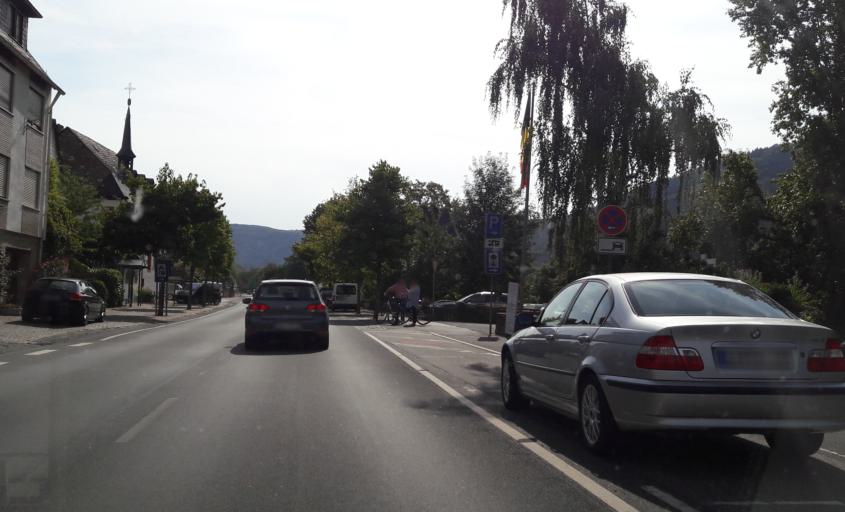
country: DE
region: Rheinland-Pfalz
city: Ediger-Eller
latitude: 50.0935
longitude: 7.1590
